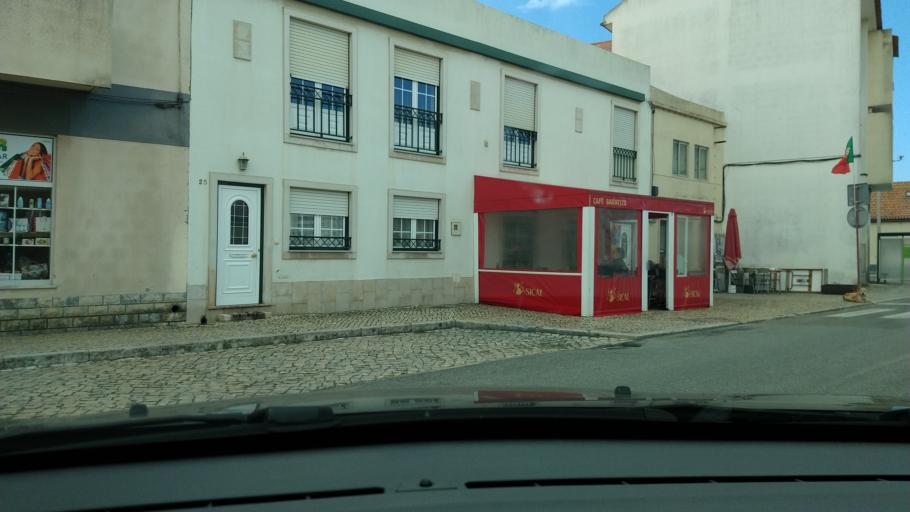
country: PT
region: Leiria
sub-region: Peniche
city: Peniche
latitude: 39.3624
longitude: -9.3923
